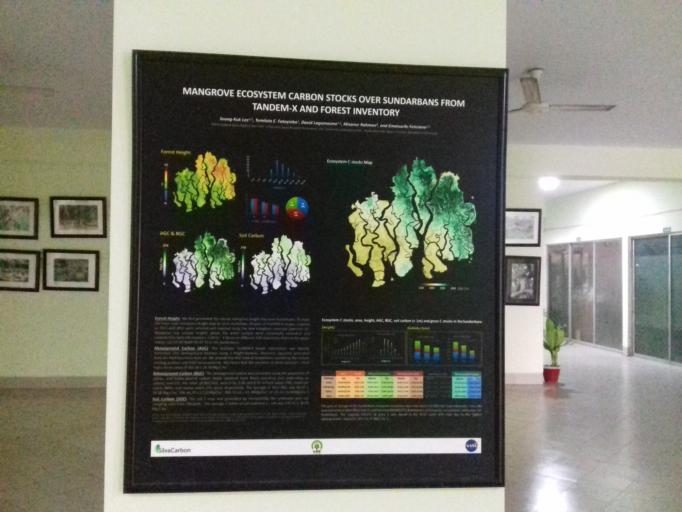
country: BD
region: Dhaka
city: Azimpur
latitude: 23.7783
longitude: 90.3789
